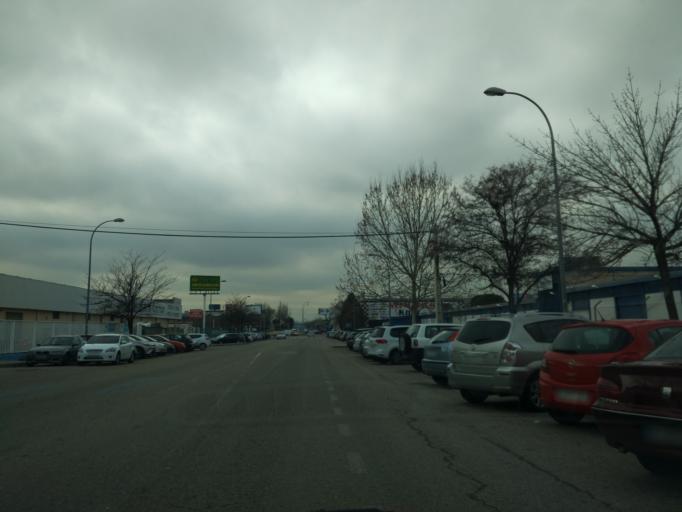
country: ES
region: Madrid
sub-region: Provincia de Madrid
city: Torrejon de Ardoz
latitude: 40.4533
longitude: -3.5051
